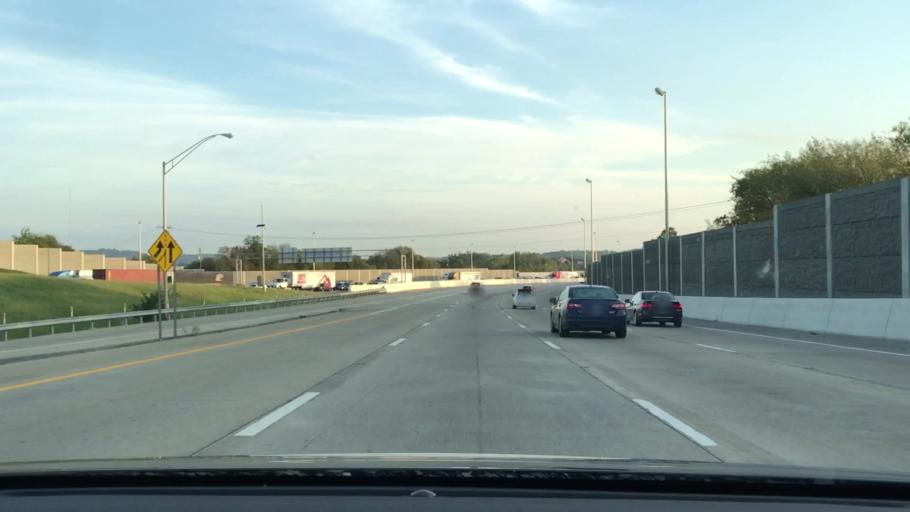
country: US
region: Tennessee
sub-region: Davidson County
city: Nashville
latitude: 36.2268
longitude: -86.7727
